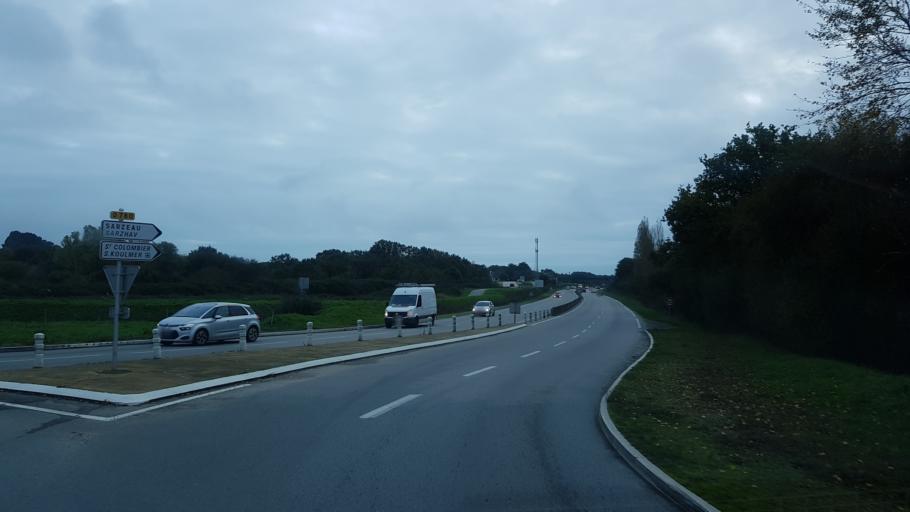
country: FR
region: Brittany
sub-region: Departement du Morbihan
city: Sarzeau
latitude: 47.5512
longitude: -2.7174
